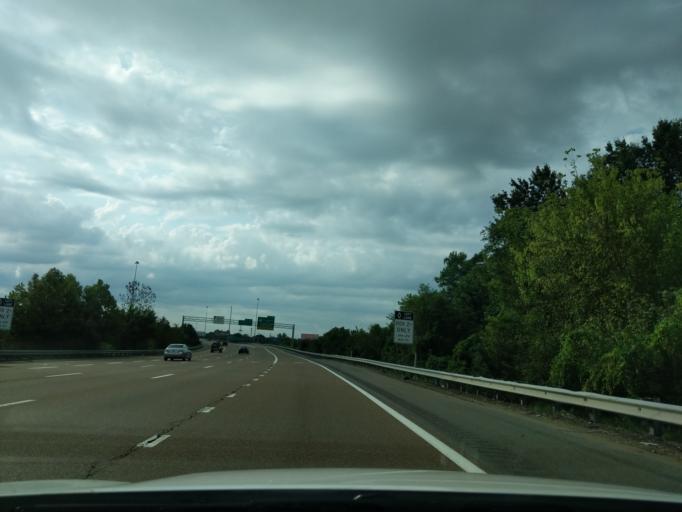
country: US
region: Tennessee
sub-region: Shelby County
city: New South Memphis
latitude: 35.0666
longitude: -90.0266
